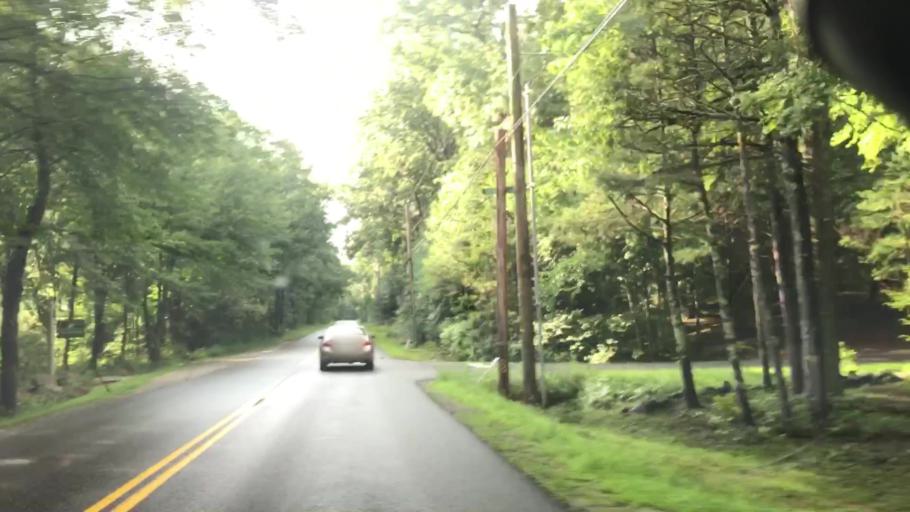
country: US
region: New Hampshire
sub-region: Hillsborough County
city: Milford
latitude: 42.8412
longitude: -71.6039
